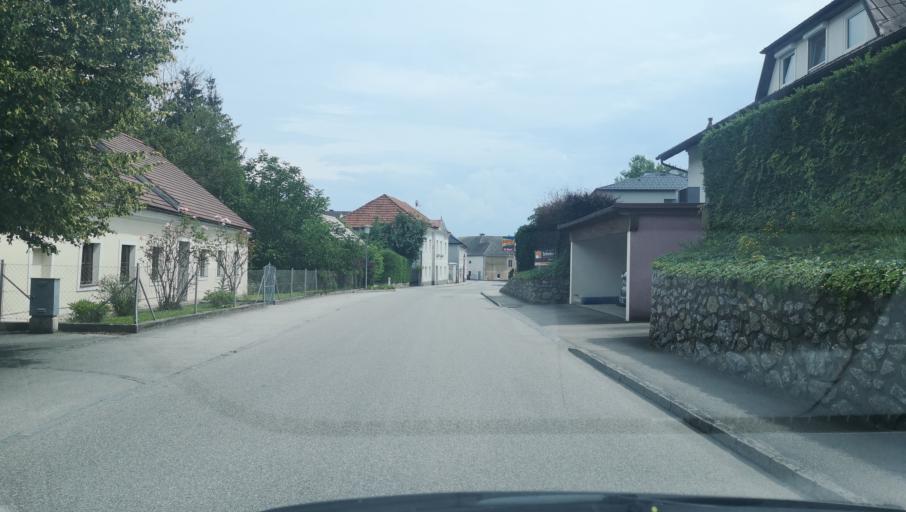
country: AT
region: Lower Austria
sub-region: Politischer Bezirk Amstetten
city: Ferschnitz
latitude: 48.0958
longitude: 14.9830
